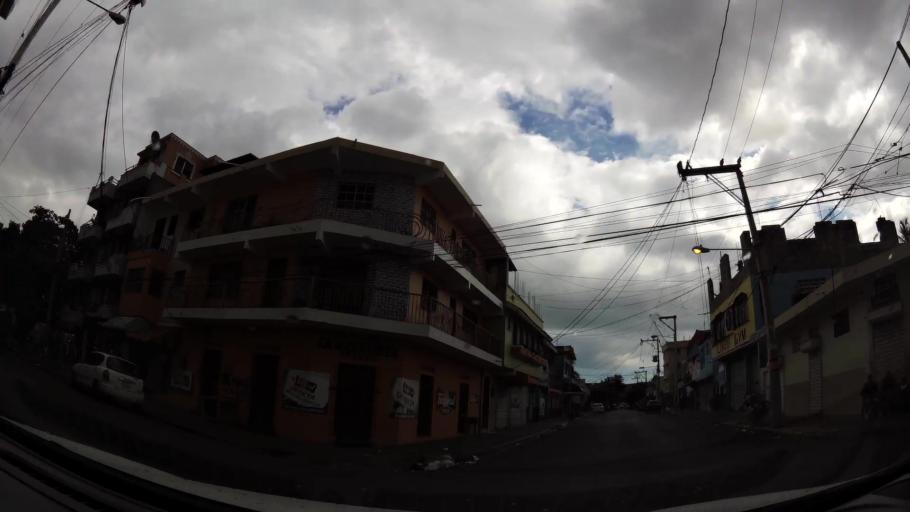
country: DO
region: Nacional
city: San Carlos
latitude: 18.4874
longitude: -69.9109
